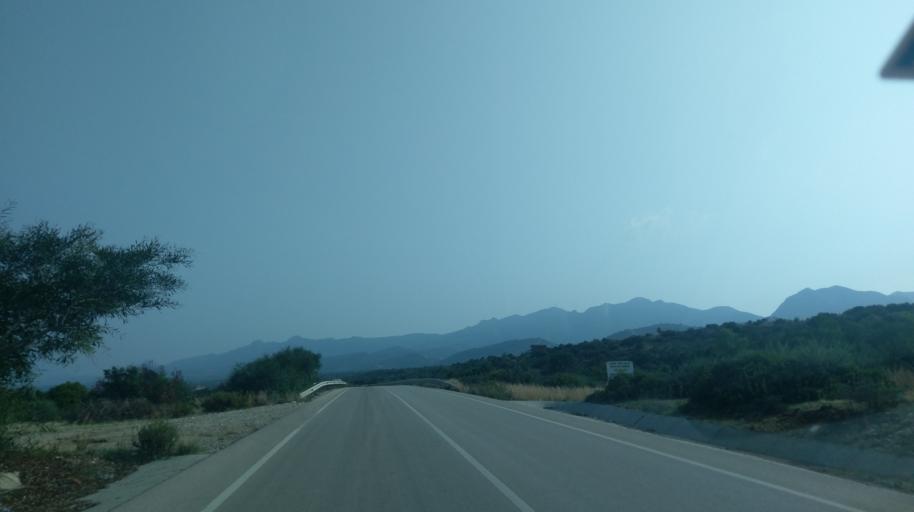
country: CY
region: Ammochostos
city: Trikomo
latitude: 35.4101
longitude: 33.8119
